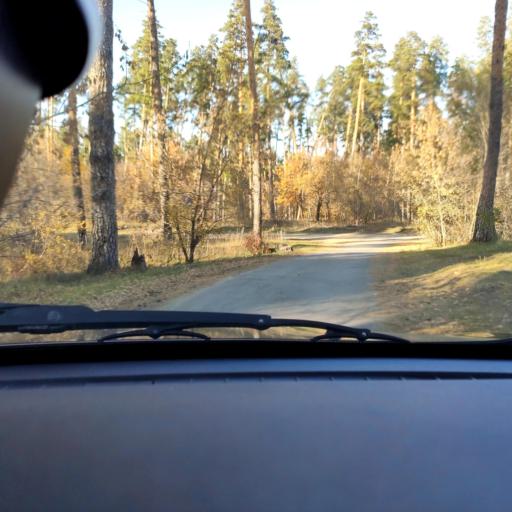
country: RU
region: Samara
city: Tol'yatti
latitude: 53.5077
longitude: 49.3883
